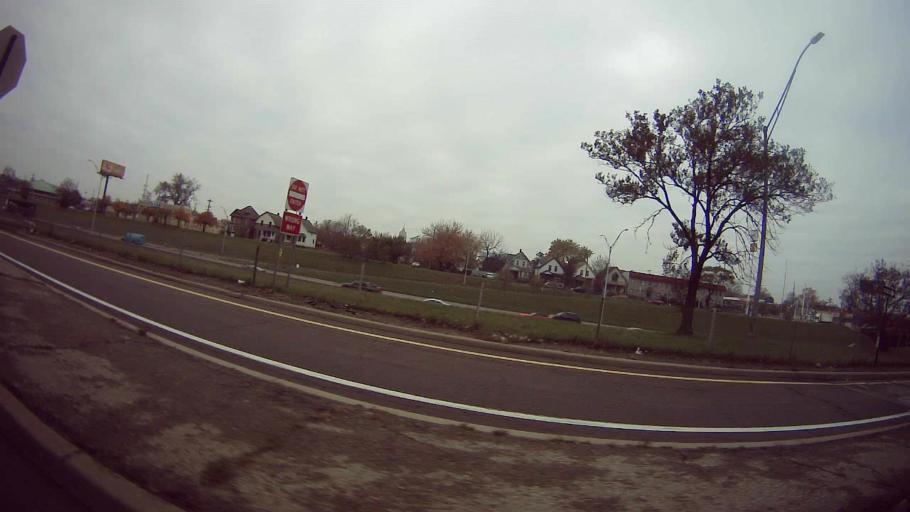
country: US
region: Michigan
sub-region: Wayne County
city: Hamtramck
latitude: 42.3775
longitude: -83.0614
